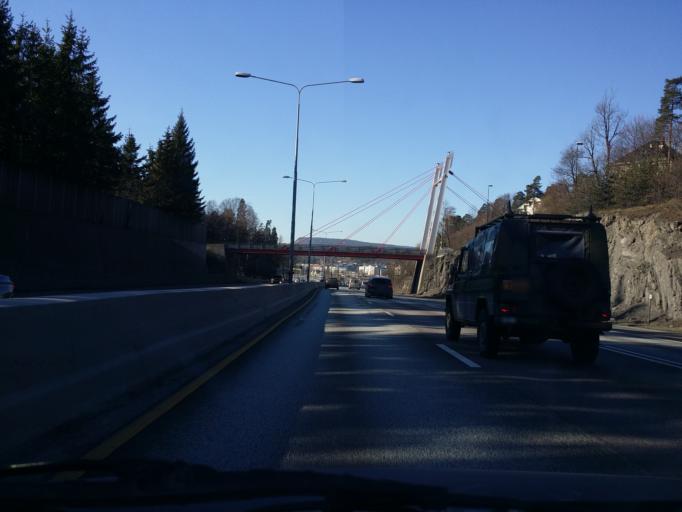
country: NO
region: Akershus
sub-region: Baerum
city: Sandvika
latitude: 59.8942
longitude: 10.5458
